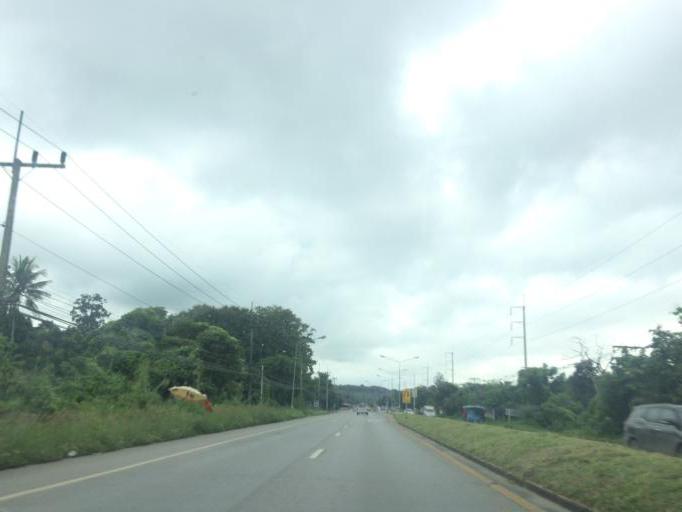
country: TH
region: Chiang Rai
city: Mae Chan
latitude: 20.1021
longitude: 99.8740
